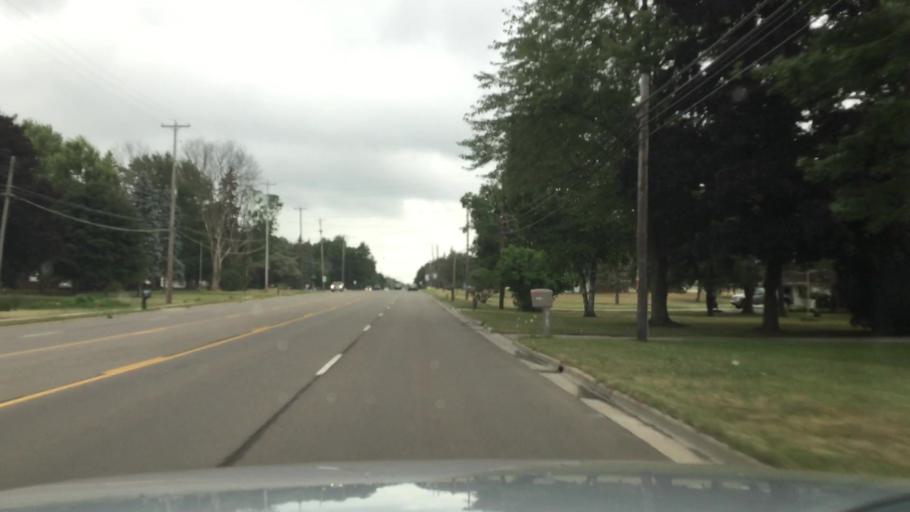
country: US
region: Michigan
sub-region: Genesee County
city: Davison
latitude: 43.0340
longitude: -83.5517
